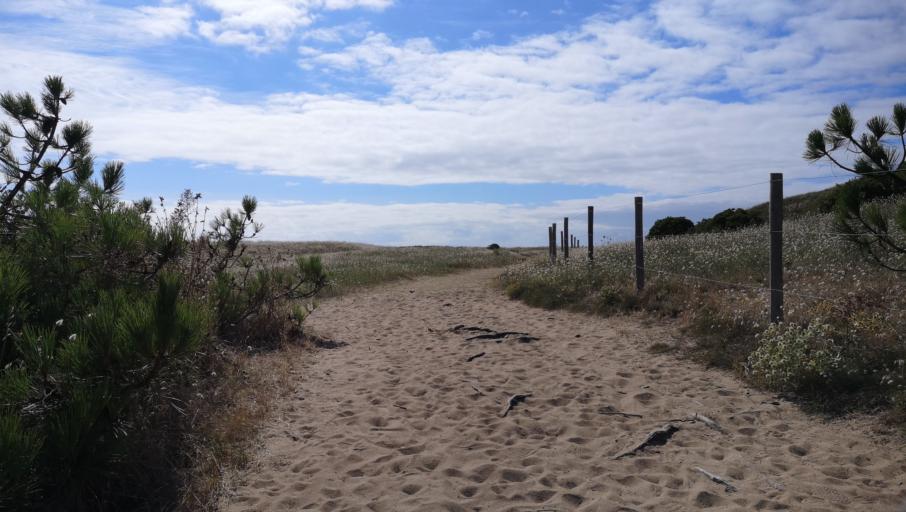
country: FR
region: Pays de la Loire
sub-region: Departement de la Vendee
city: Les Sables-d'Olonne
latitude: 46.5141
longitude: -1.8156
